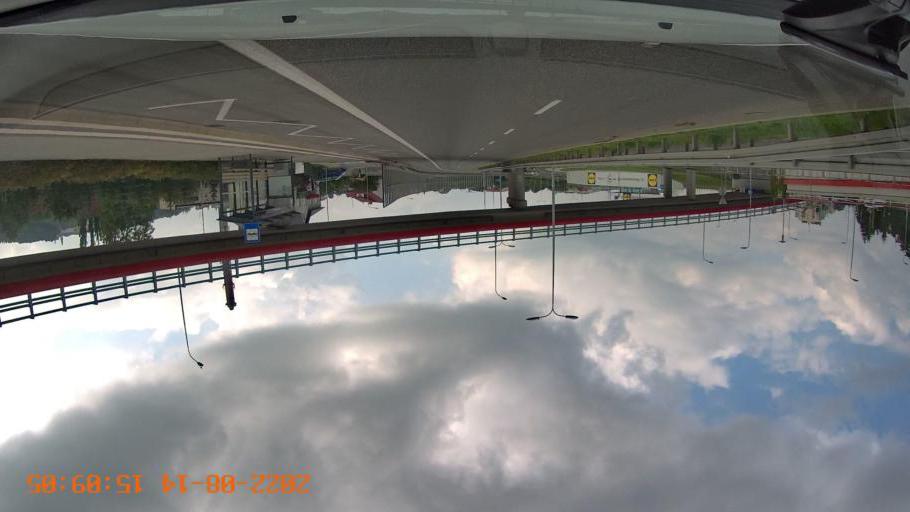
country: PL
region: Swietokrzyskie
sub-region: Powiat kielecki
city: Kielce
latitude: 50.8776
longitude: 20.5922
